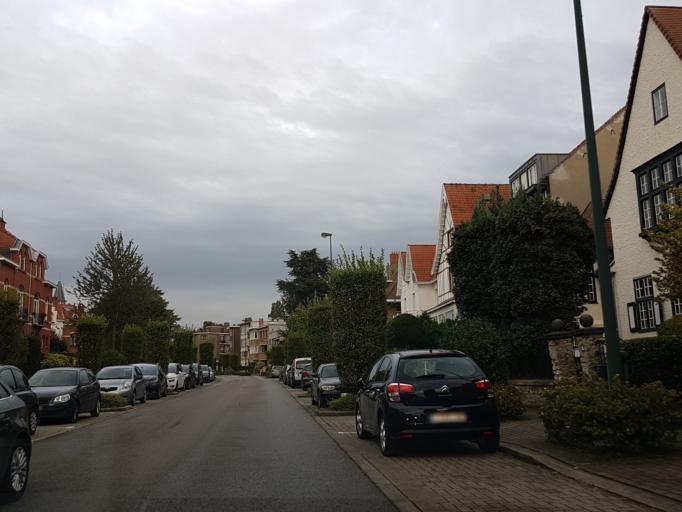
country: BE
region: Flanders
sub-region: Provincie Vlaams-Brabant
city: Kraainem
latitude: 50.8314
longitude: 4.4413
